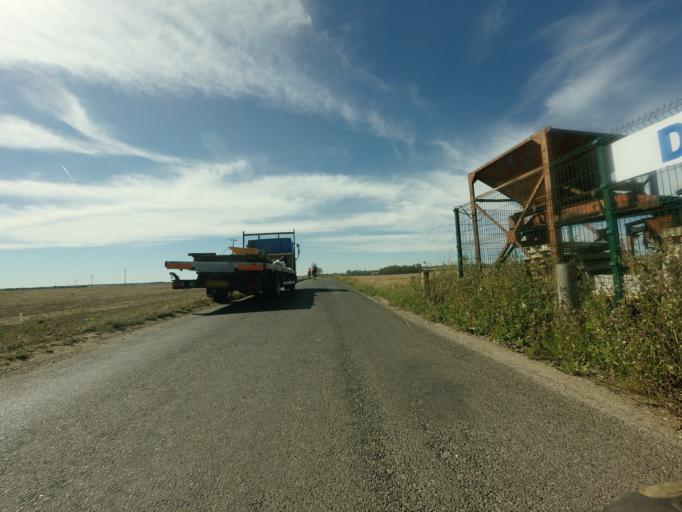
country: GB
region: England
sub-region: Kent
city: Birchington-on-Sea
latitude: 51.3418
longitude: 1.2677
